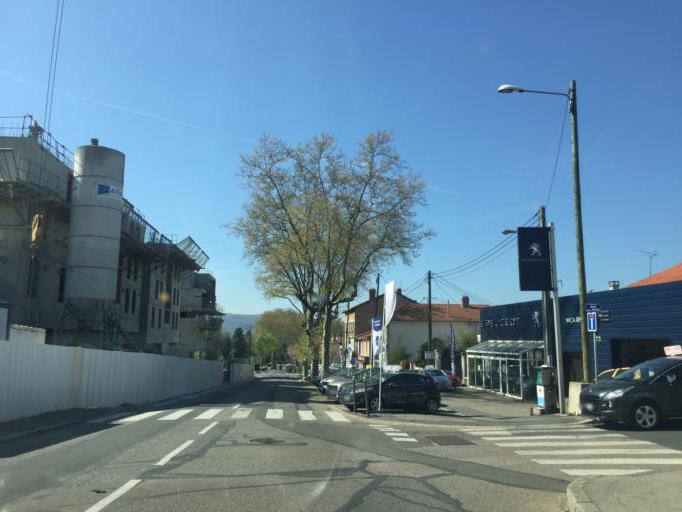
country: FR
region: Rhone-Alpes
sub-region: Departement du Rhone
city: Sathonay-Camp
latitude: 45.8245
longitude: 4.8745
